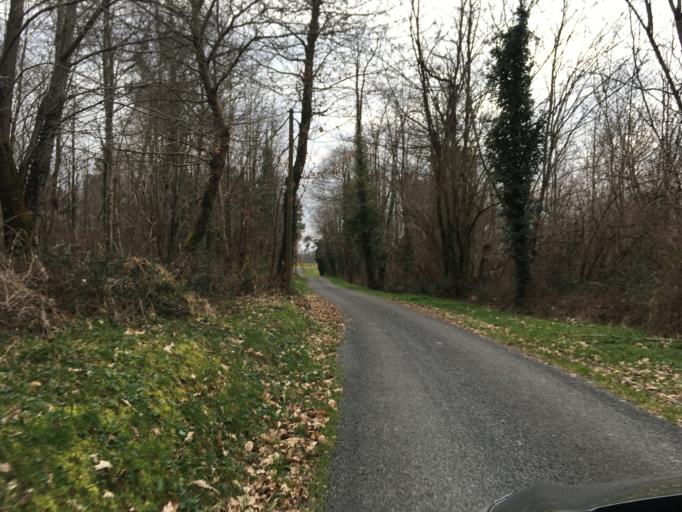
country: FR
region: Aquitaine
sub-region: Departement de la Gironde
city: Saint-Ciers-sur-Gironde
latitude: 45.3199
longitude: -0.6002
